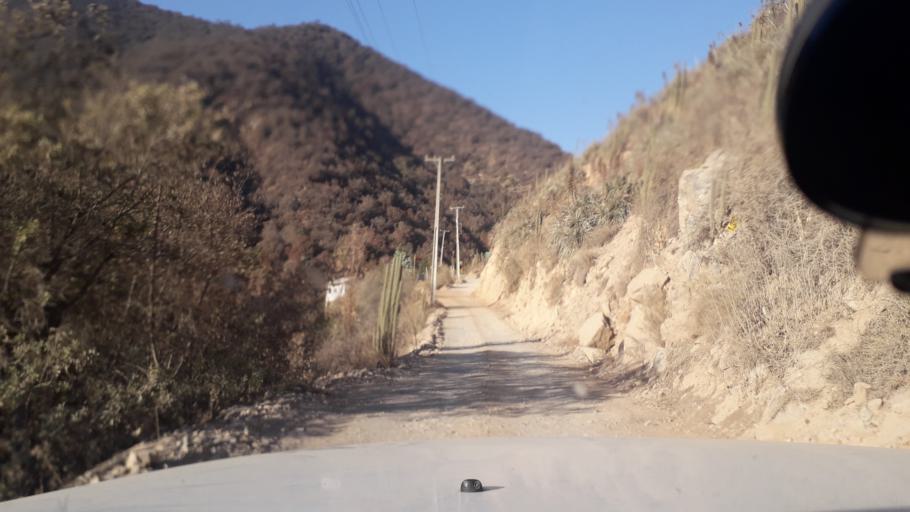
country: CL
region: Valparaiso
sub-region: Provincia de Marga Marga
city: Limache
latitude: -33.0524
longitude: -71.0796
